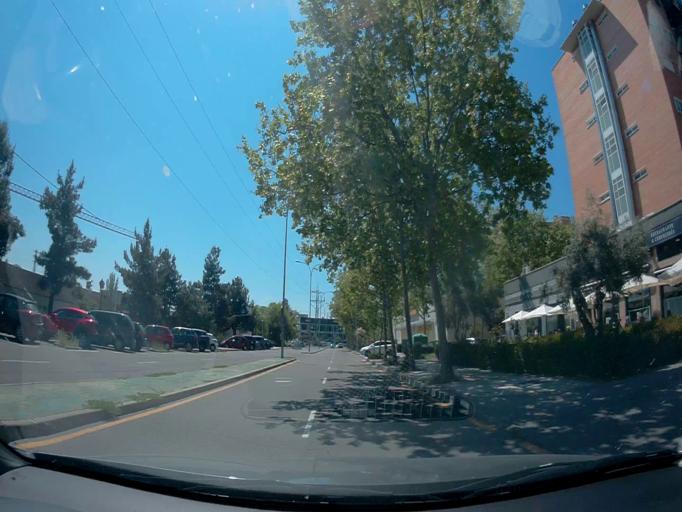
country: ES
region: Madrid
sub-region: Provincia de Madrid
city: Alcorcon
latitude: 40.3450
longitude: -3.8074
